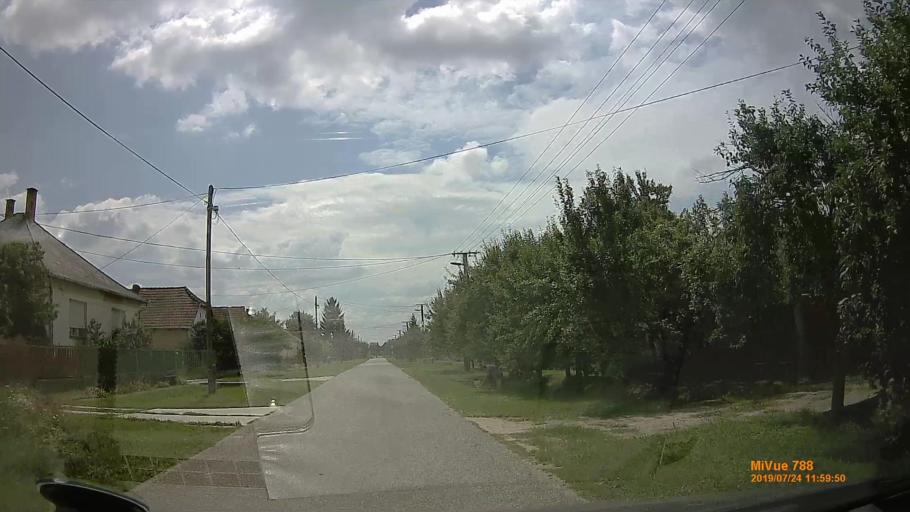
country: HU
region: Szabolcs-Szatmar-Bereg
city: Tarpa
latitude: 48.2008
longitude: 22.4512
